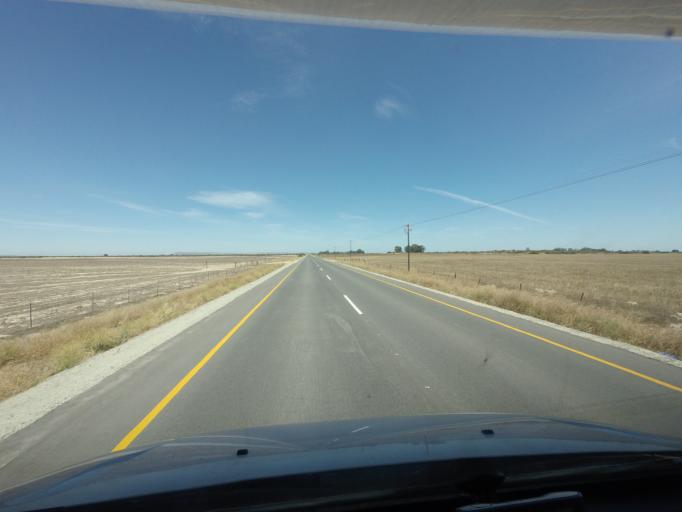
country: ZA
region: Western Cape
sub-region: West Coast District Municipality
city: Vredenburg
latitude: -32.7966
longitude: 18.2612
